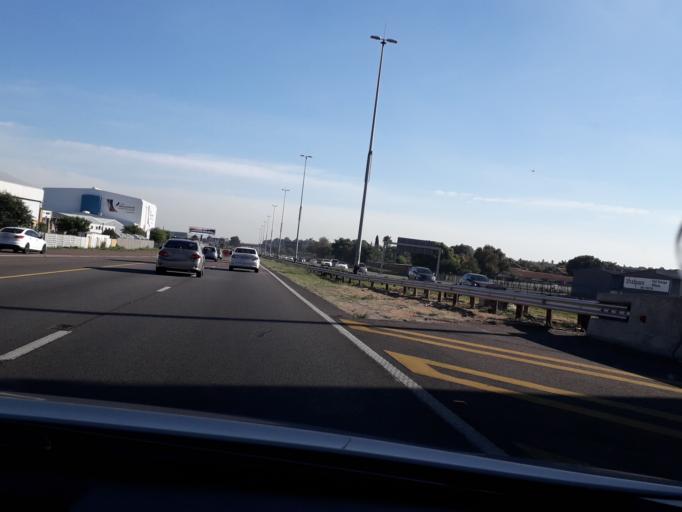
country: ZA
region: Gauteng
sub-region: City of Tshwane Metropolitan Municipality
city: Centurion
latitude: -25.8732
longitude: 28.1698
